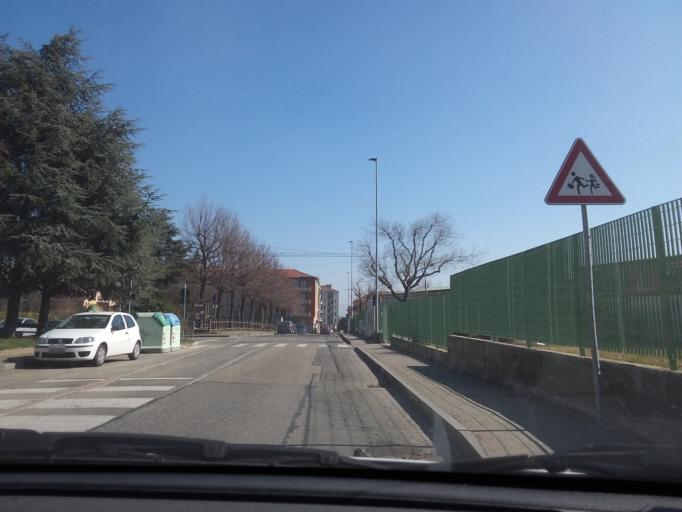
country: IT
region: Piedmont
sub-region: Provincia di Torino
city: Rivoli
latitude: 45.0694
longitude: 7.5413
